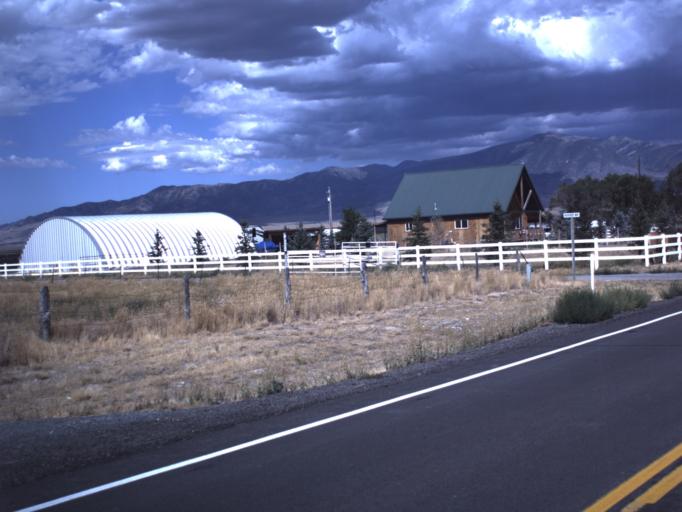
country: US
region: Utah
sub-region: Tooele County
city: Tooele
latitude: 40.3366
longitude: -112.4444
